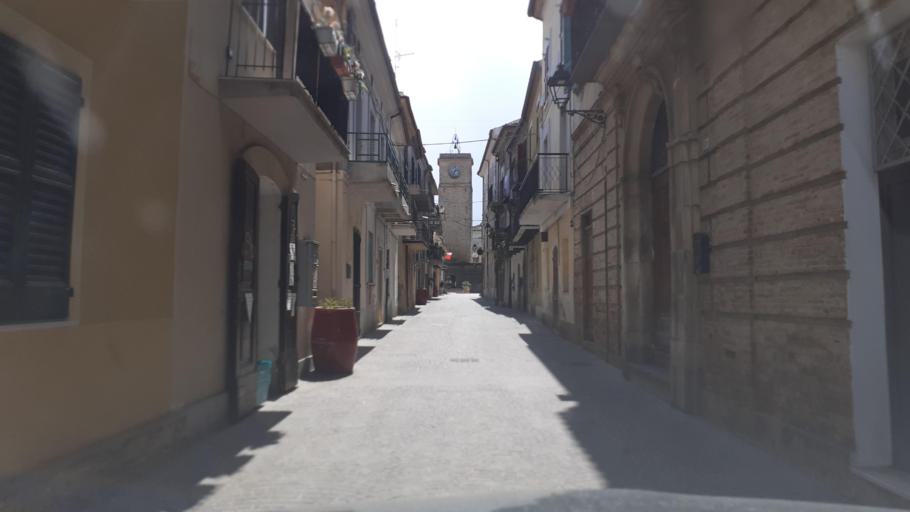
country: IT
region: Abruzzo
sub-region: Provincia di Chieti
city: Rocca San Giovanni
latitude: 42.2514
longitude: 14.4656
